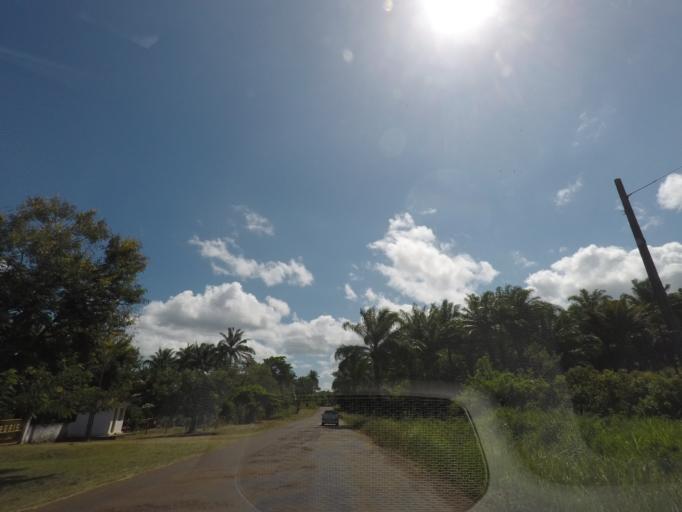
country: BR
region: Bahia
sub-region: Taperoa
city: Taperoa
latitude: -13.5518
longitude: -39.1011
